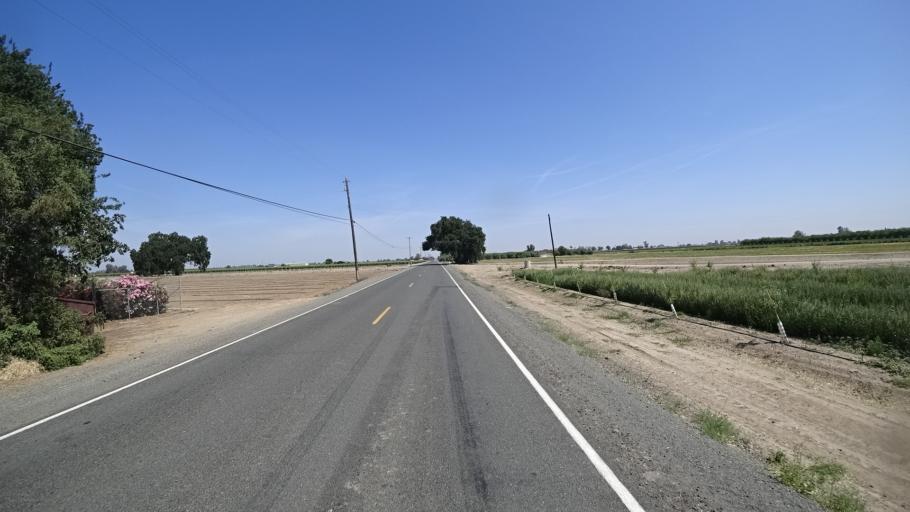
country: US
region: California
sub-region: Fresno County
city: Riverdale
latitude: 36.3598
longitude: -119.8513
